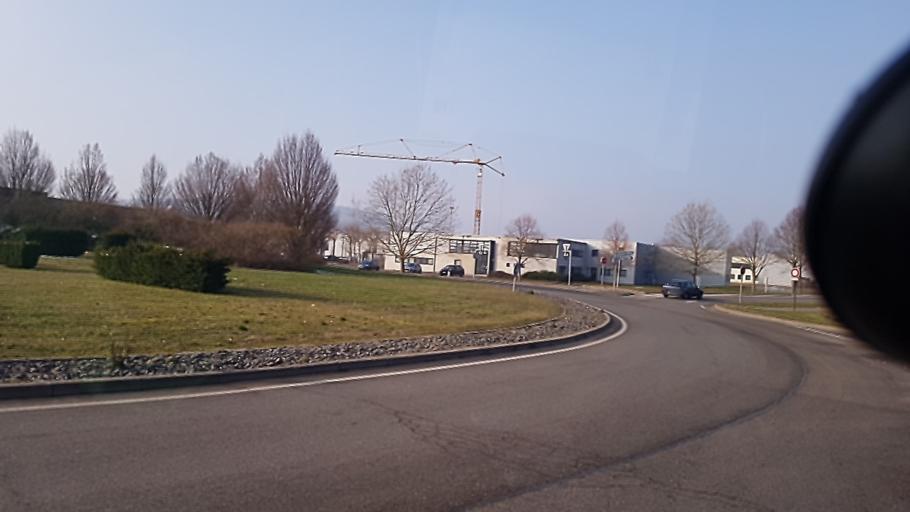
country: FR
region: Alsace
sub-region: Departement du Bas-Rhin
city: Bischoffsheim
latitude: 48.5039
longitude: 7.4972
